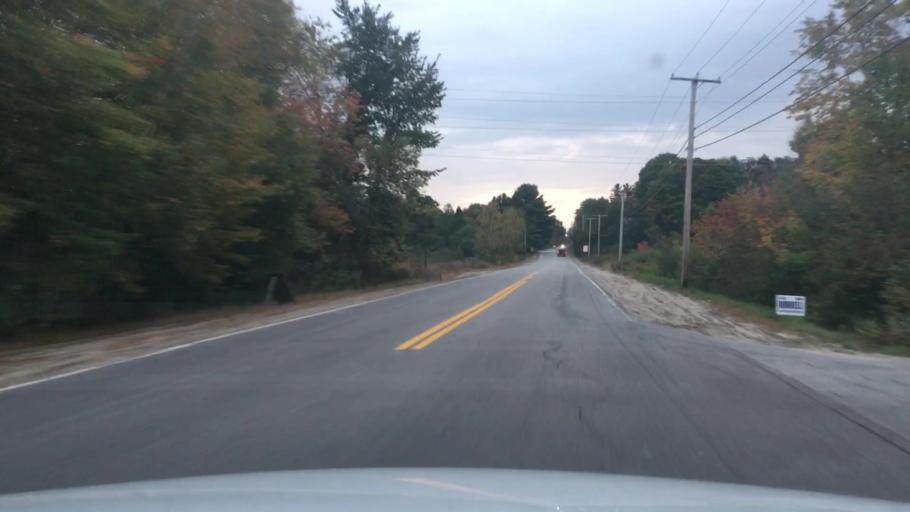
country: US
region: Maine
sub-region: York County
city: Buxton
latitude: 43.6397
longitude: -70.5233
